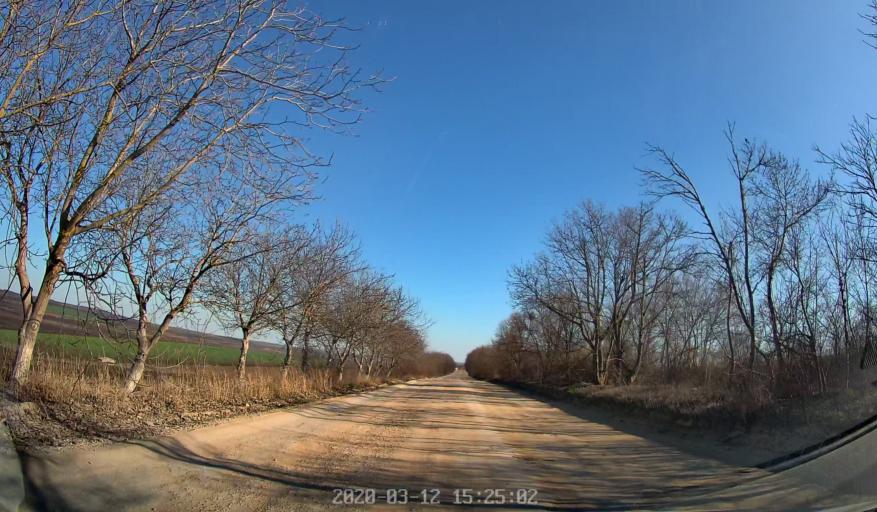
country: MD
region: Chisinau
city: Ciorescu
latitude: 47.1843
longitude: 28.9163
